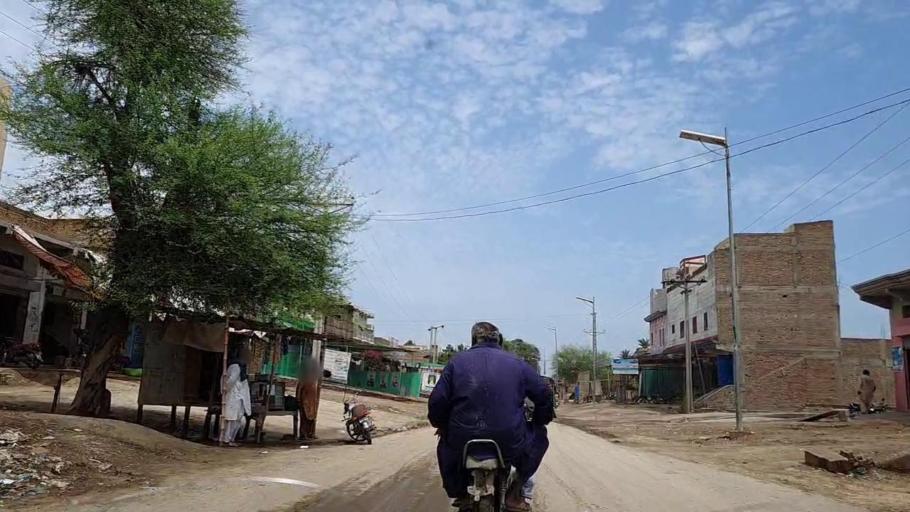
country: PK
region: Sindh
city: Naushahro Firoz
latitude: 26.8435
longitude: 68.1054
